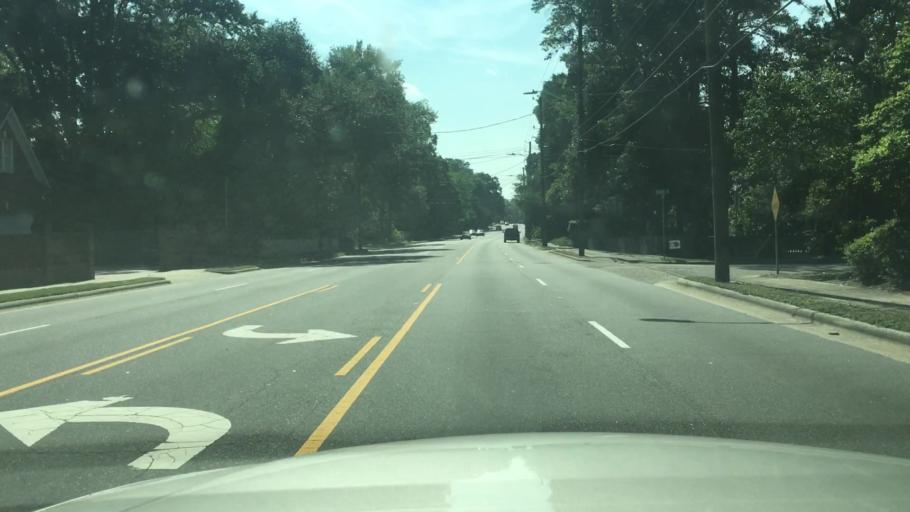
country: US
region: North Carolina
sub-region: Cumberland County
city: Fayetteville
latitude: 35.0594
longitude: -78.9100
